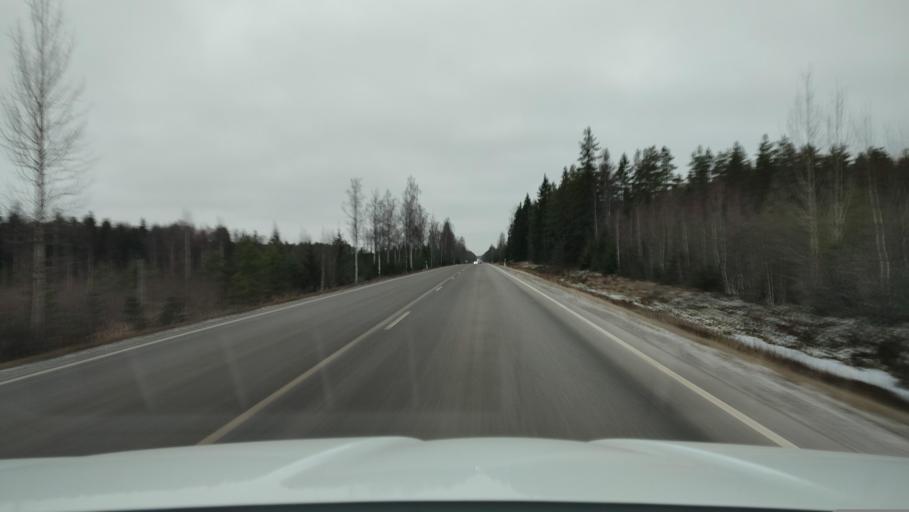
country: FI
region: Ostrobothnia
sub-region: Sydosterbotten
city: Naerpes
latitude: 62.5057
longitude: 21.4509
